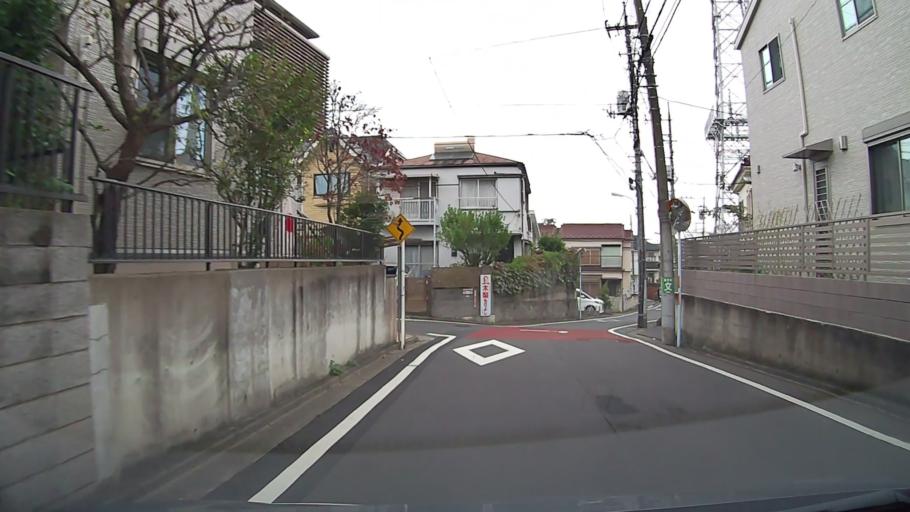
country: JP
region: Tokyo
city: Tokyo
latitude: 35.6877
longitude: 139.6302
